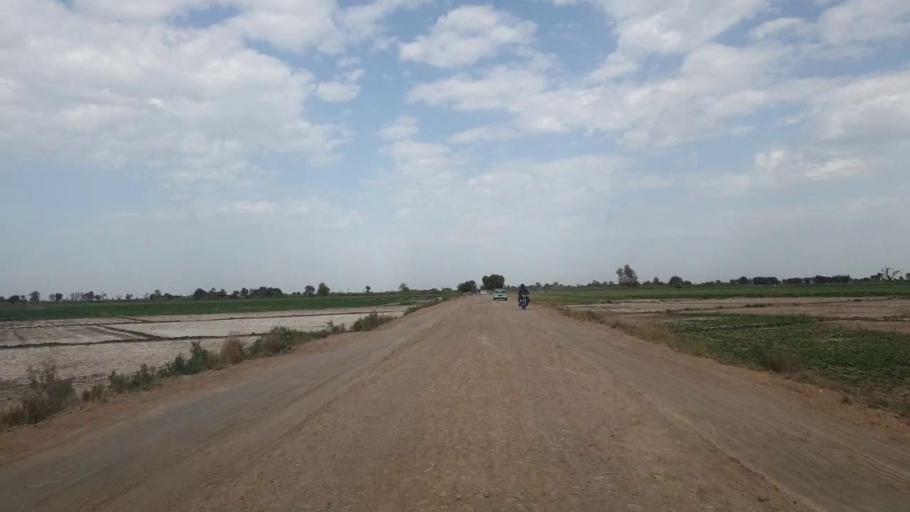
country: PK
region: Sindh
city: Hala
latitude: 25.9615
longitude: 68.4678
